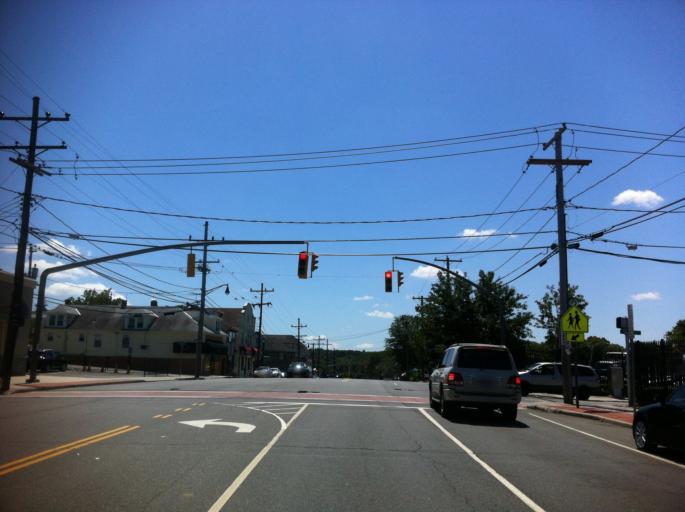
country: US
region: New York
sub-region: Nassau County
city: Glen Cove
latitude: 40.8590
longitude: -73.6205
